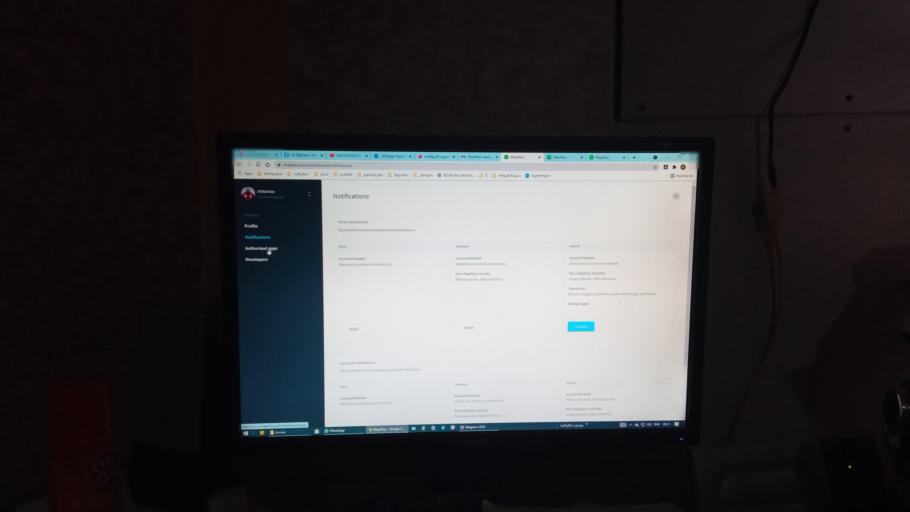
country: GE
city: Tsqnet'i
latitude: 41.6977
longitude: 44.7050
